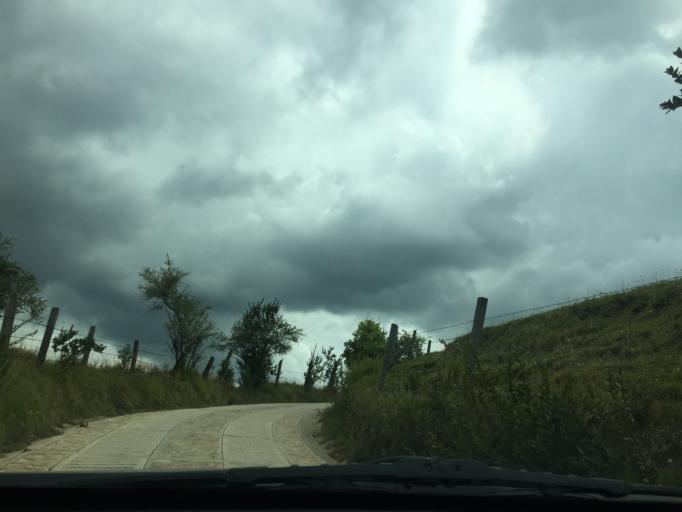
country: CO
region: Cundinamarca
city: Cogua
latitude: 5.0549
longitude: -74.0010
